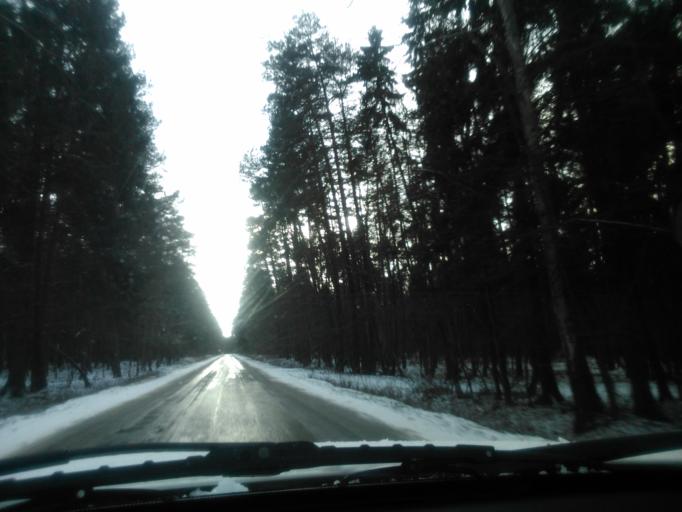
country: PL
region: Kujawsko-Pomorskie
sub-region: Powiat golubsko-dobrzynski
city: Golub-Dobrzyn
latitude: 53.1657
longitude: 19.1316
